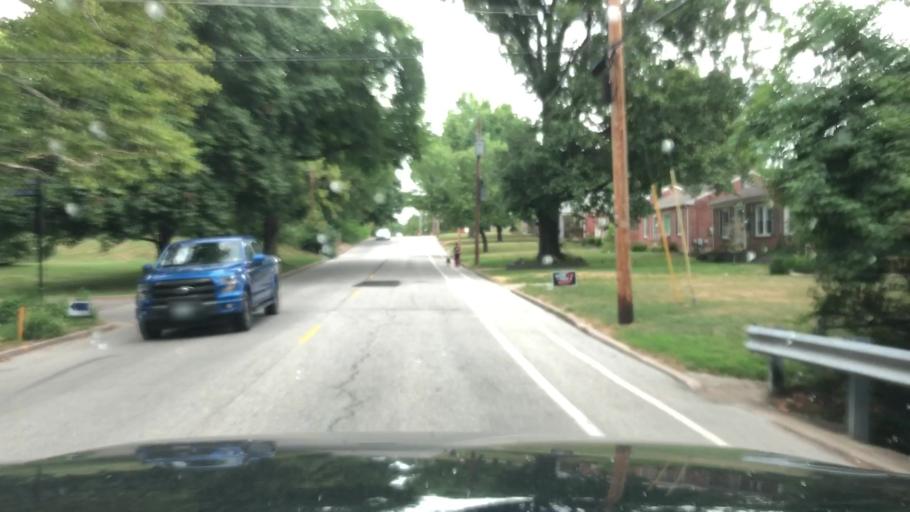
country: US
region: Missouri
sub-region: Saint Charles County
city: Saint Charles
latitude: 38.7925
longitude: -90.4991
